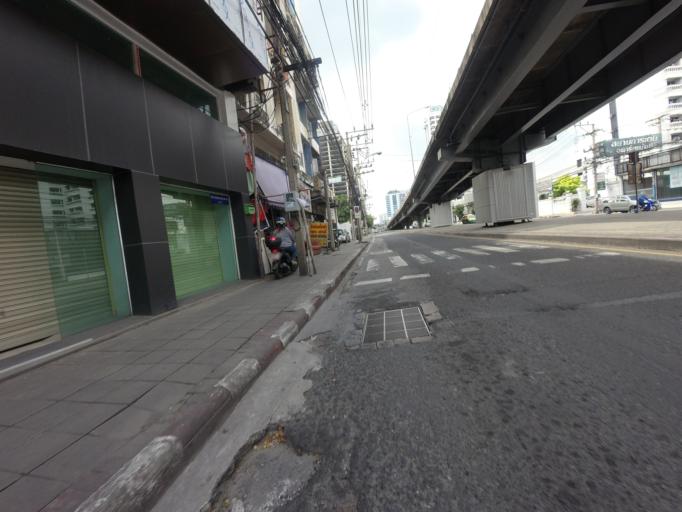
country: TH
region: Bangkok
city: Watthana
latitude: 13.7419
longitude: 100.5964
